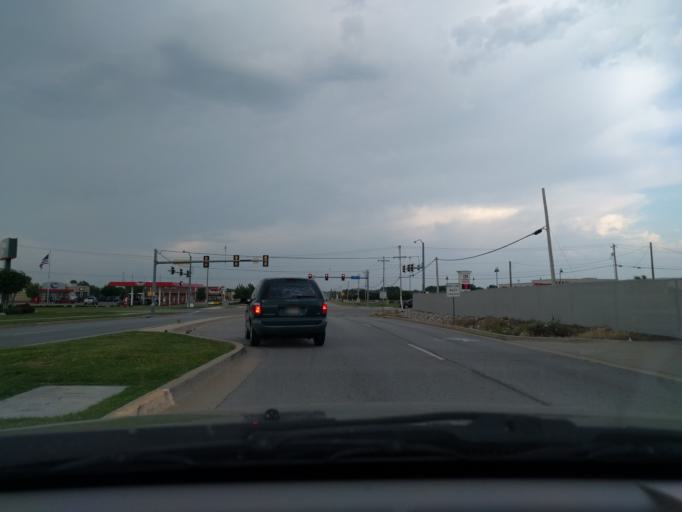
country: US
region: Oklahoma
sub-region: Tulsa County
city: Broken Arrow
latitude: 36.0755
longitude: -95.7806
